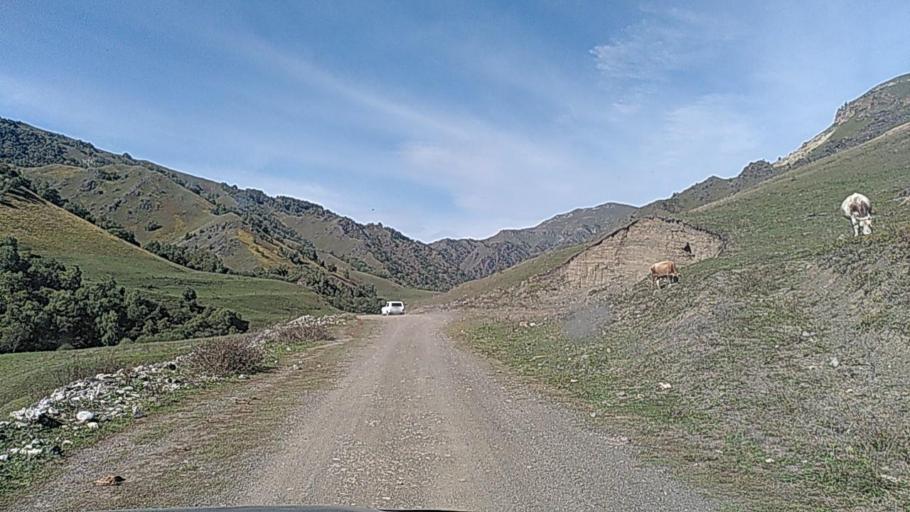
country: RU
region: Kabardino-Balkariya
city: Kamennomostskoye
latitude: 43.7186
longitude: 42.8816
